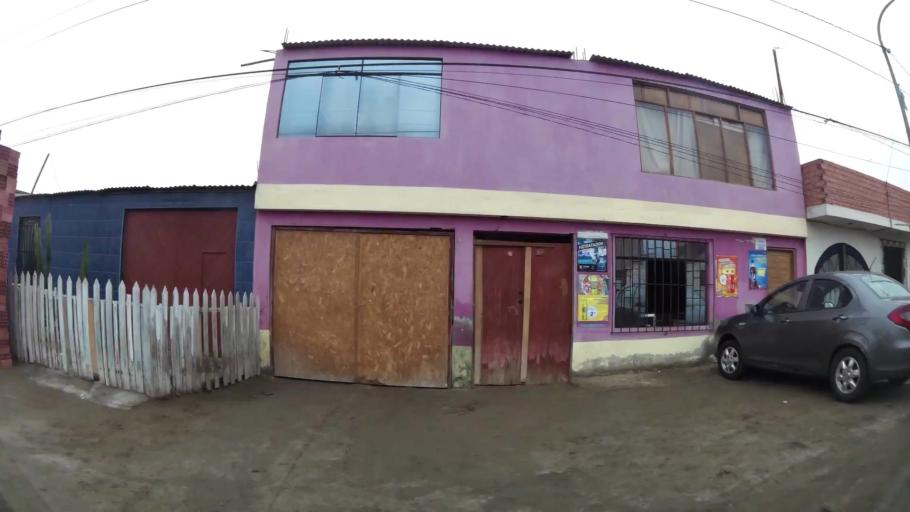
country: PE
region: Lima
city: Ventanilla
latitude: -11.8776
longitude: -77.1356
